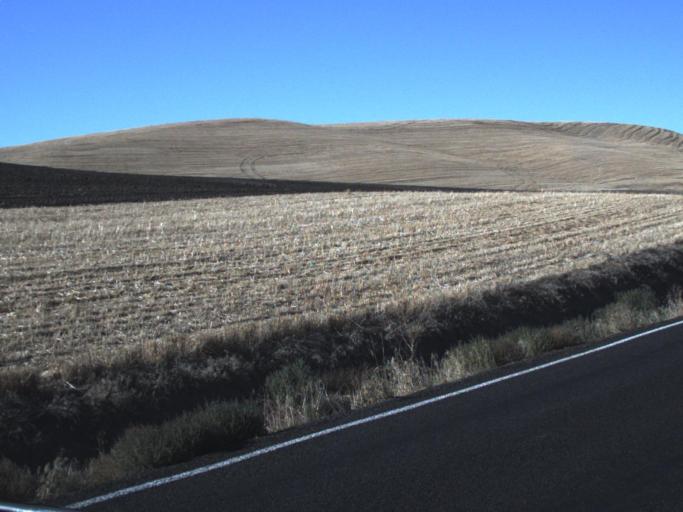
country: US
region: Washington
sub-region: Walla Walla County
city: Walla Walla
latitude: 46.1858
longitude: -118.3838
